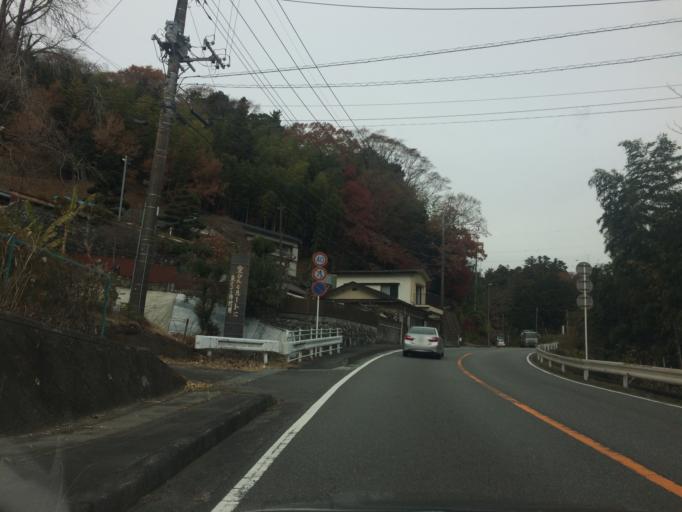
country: JP
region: Shizuoka
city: Fujinomiya
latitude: 35.3191
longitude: 138.4395
